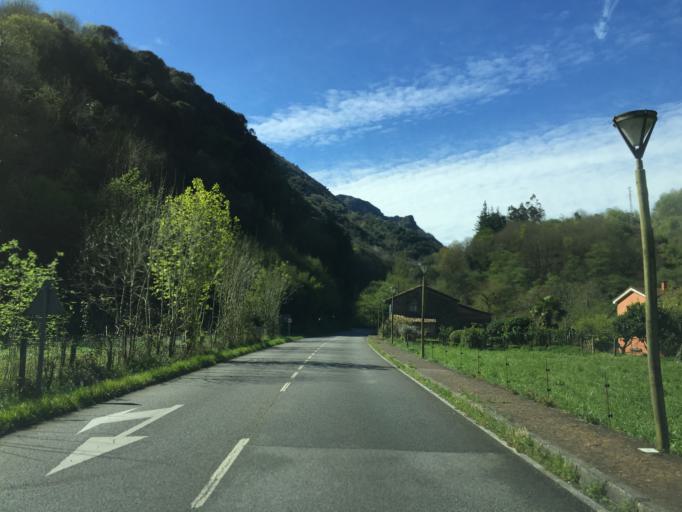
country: ES
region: Asturias
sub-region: Province of Asturias
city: Proaza
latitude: 43.2890
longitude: -5.9830
